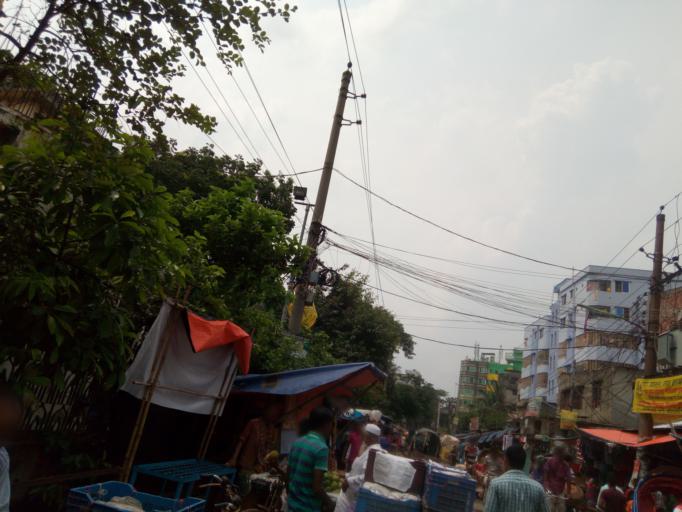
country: BD
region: Dhaka
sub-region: Dhaka
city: Dhaka
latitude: 23.7143
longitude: 90.3914
